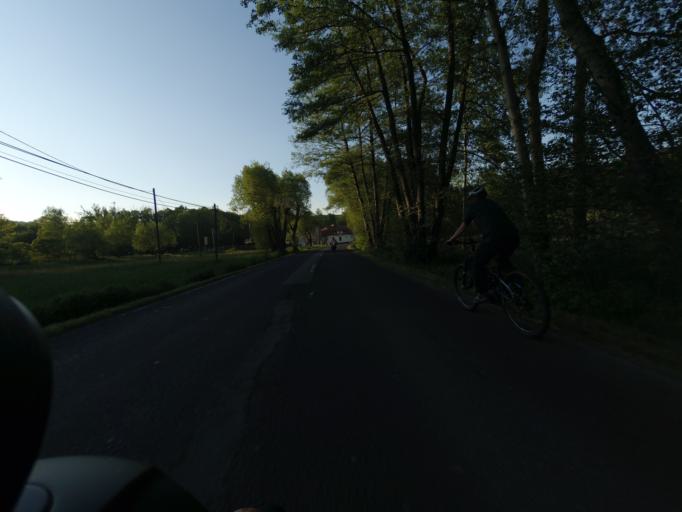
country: DE
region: Saxony
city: Kreischa
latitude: 50.9657
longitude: 13.7777
